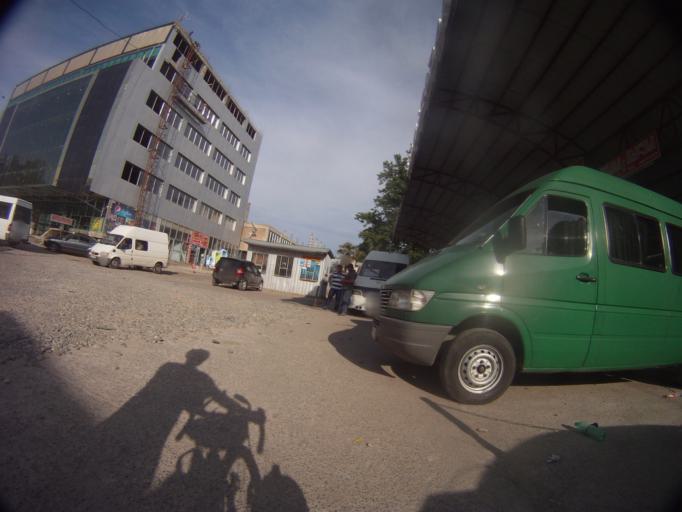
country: GE
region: Imereti
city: Kutaisi
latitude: 42.2582
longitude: 42.6679
